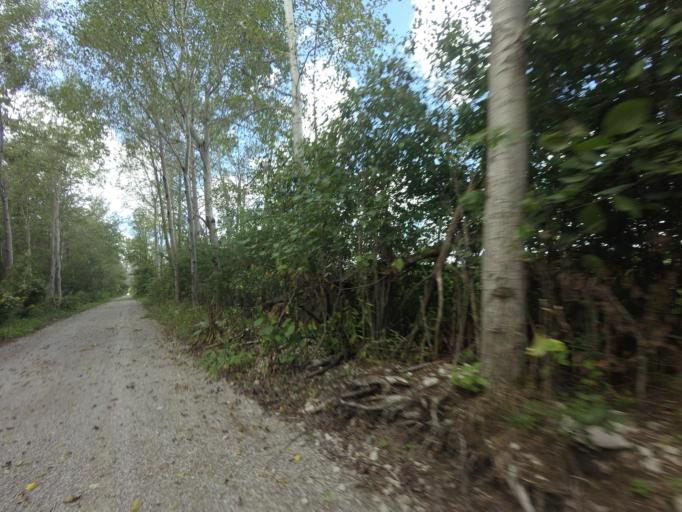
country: CA
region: Ontario
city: Huron East
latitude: 43.6380
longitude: -81.1970
